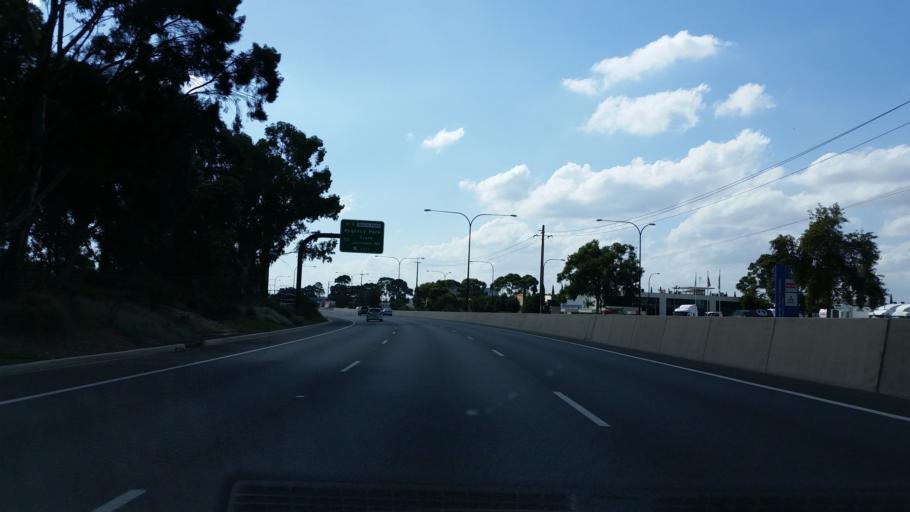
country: AU
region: South Australia
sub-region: Port Adelaide Enfield
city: Blair Athol
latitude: -34.8651
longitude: 138.5703
